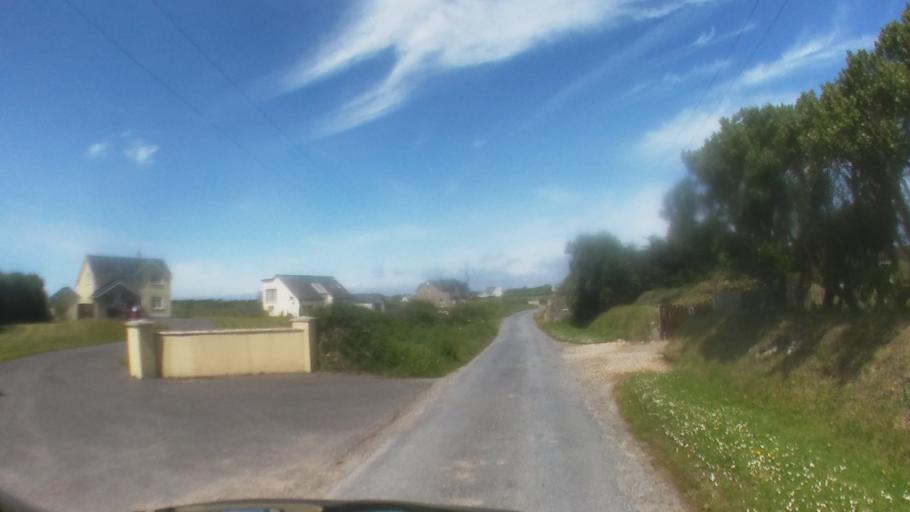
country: IE
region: Leinster
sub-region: Loch Garman
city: Loch Garman
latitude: 52.1864
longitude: -6.5378
